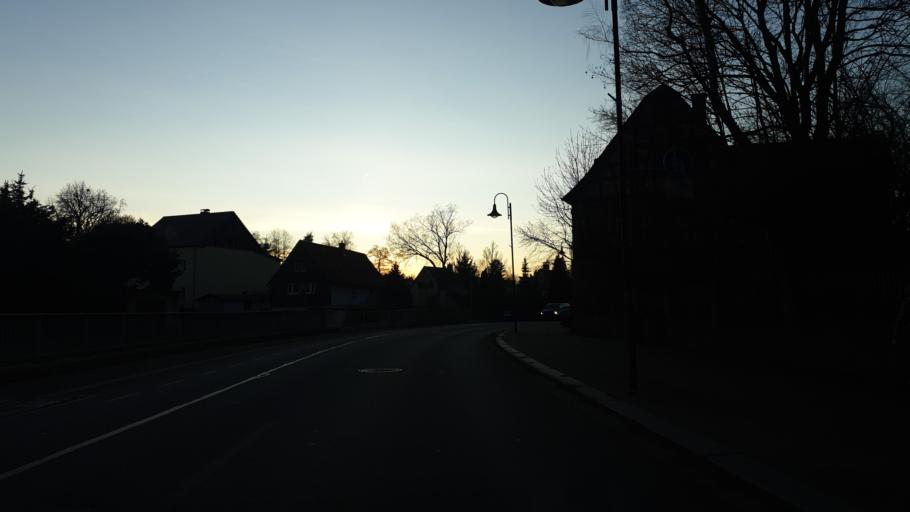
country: DE
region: Saxony
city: Oberlungwitz
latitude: 50.7835
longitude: 12.7118
